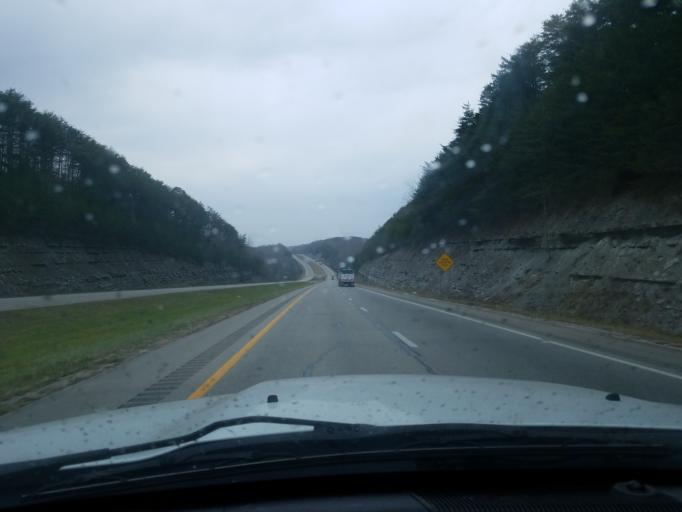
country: US
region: Kentucky
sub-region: Rowan County
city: Morehead
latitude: 38.1857
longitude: -83.5169
